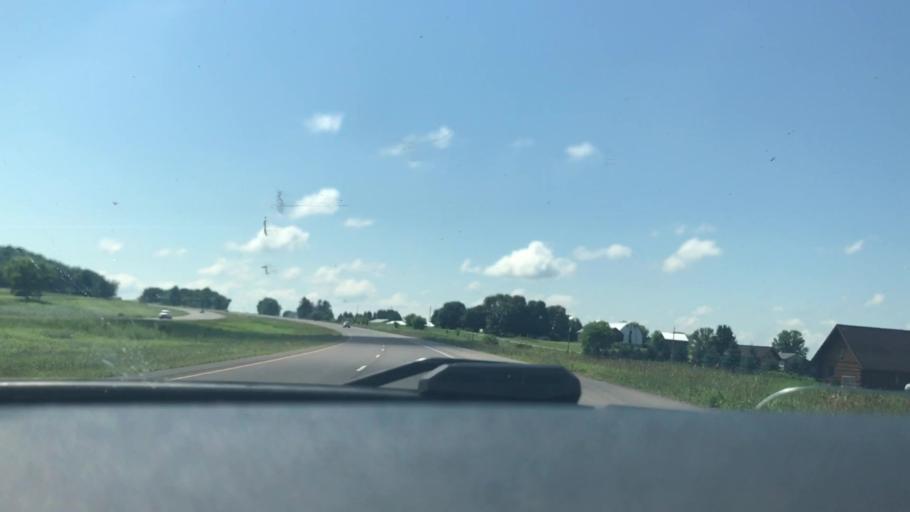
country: US
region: Wisconsin
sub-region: Chippewa County
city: Bloomer
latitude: 45.0513
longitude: -91.4657
